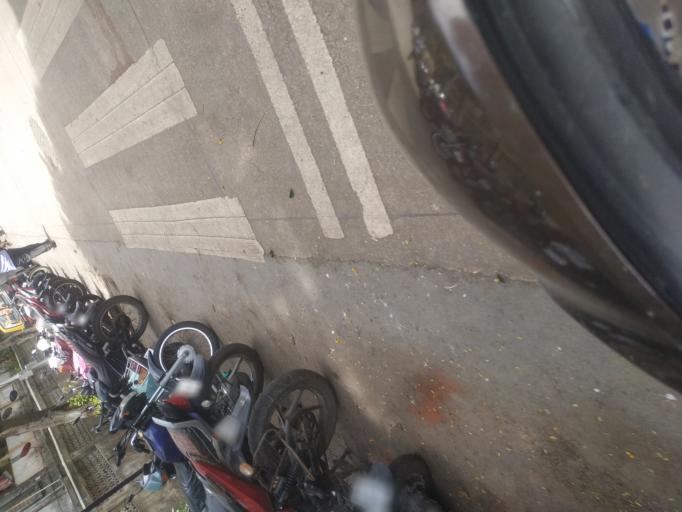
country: IN
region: Maharashtra
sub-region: Mumbai Suburban
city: Mumbai
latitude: 18.9947
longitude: 72.8413
